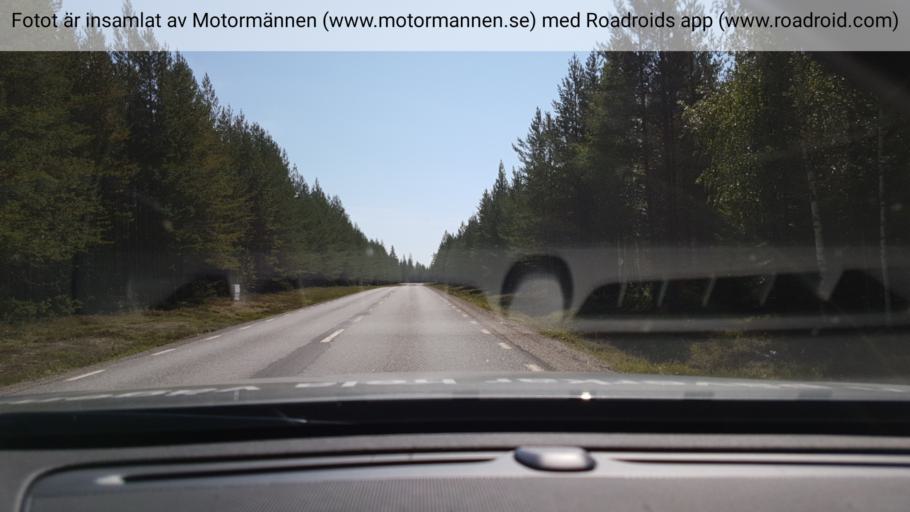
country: SE
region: Vaesterbotten
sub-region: Vindelns Kommun
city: Vindeln
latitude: 64.2515
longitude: 19.6387
